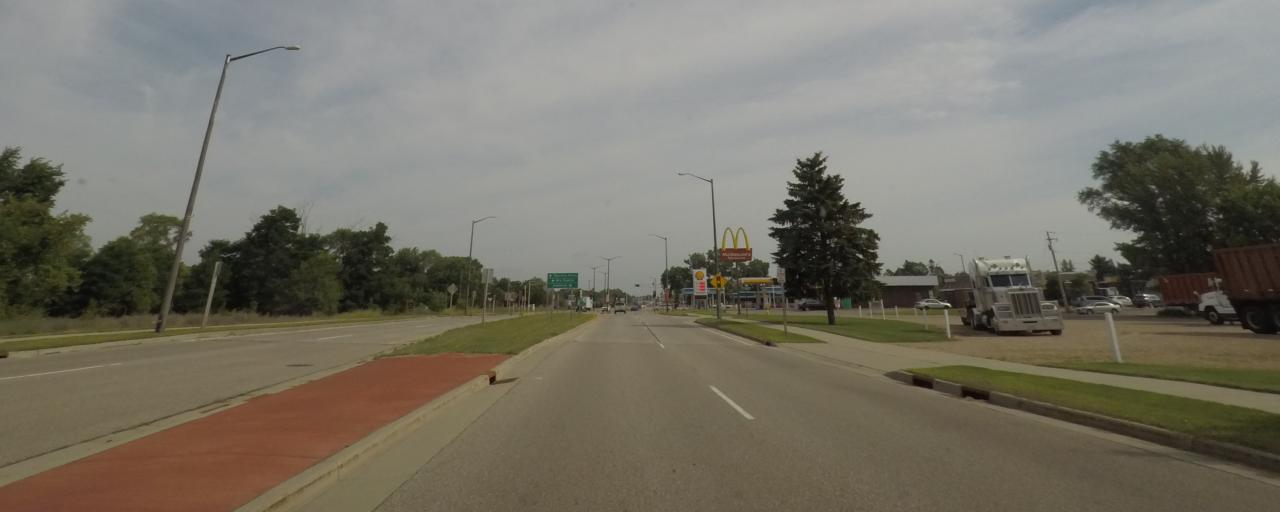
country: US
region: Wisconsin
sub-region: Portage County
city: Plover
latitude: 44.4521
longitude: -89.5441
